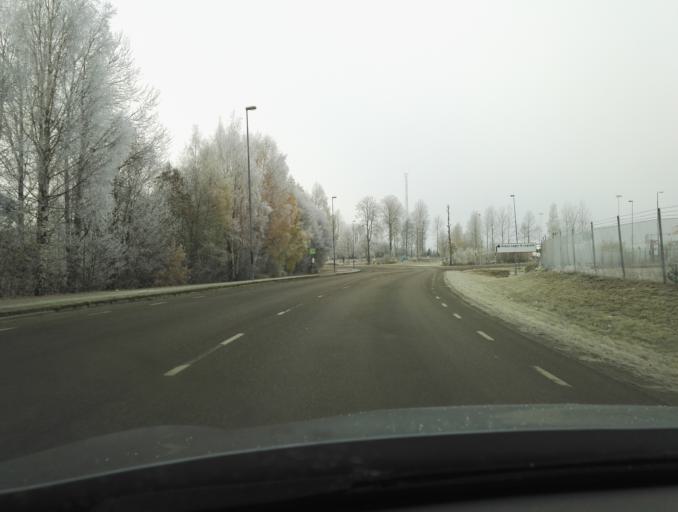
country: SE
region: Kronoberg
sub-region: Vaxjo Kommun
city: Vaexjoe
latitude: 56.8849
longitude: 14.7352
